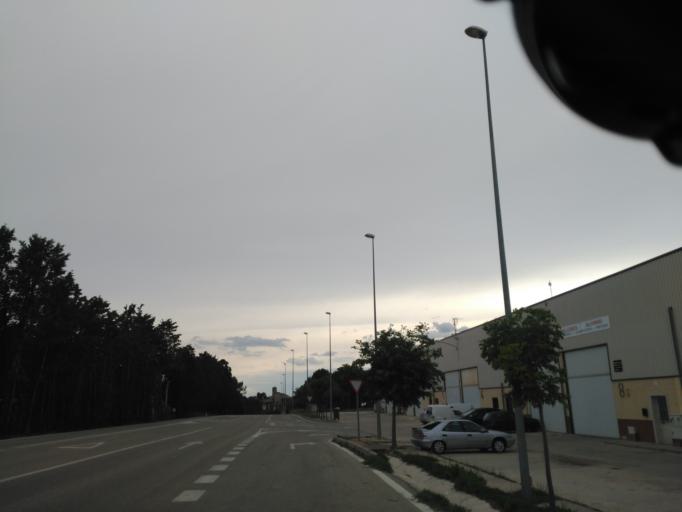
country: ES
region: Madrid
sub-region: Provincia de Madrid
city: Santorcaz
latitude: 40.4762
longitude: -3.2239
